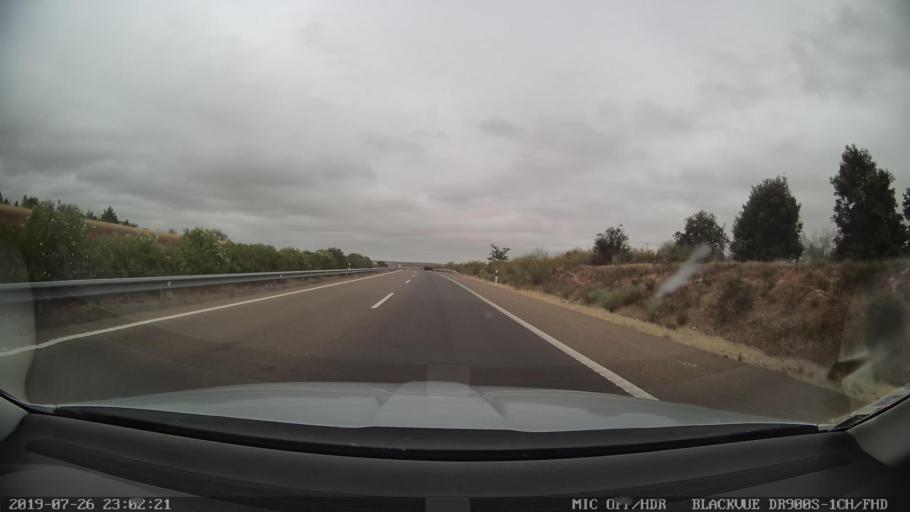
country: ES
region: Extremadura
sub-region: Provincia de Badajoz
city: Merida
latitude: 38.9448
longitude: -6.3101
